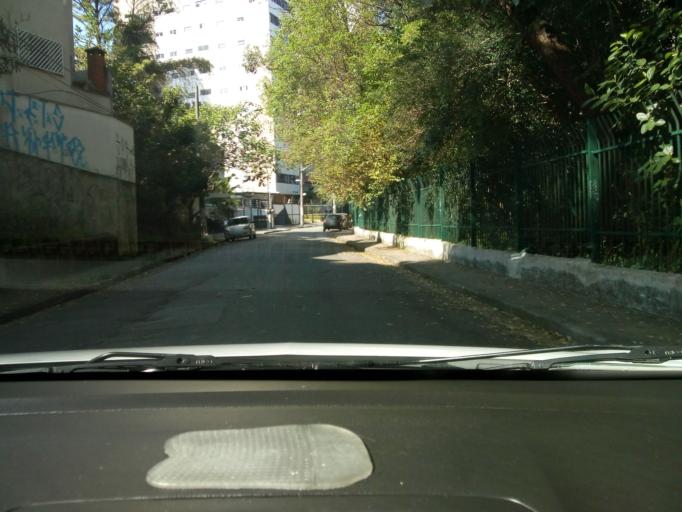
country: BR
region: Sao Paulo
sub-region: Sao Paulo
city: Sao Paulo
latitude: -23.5758
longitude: -46.6272
